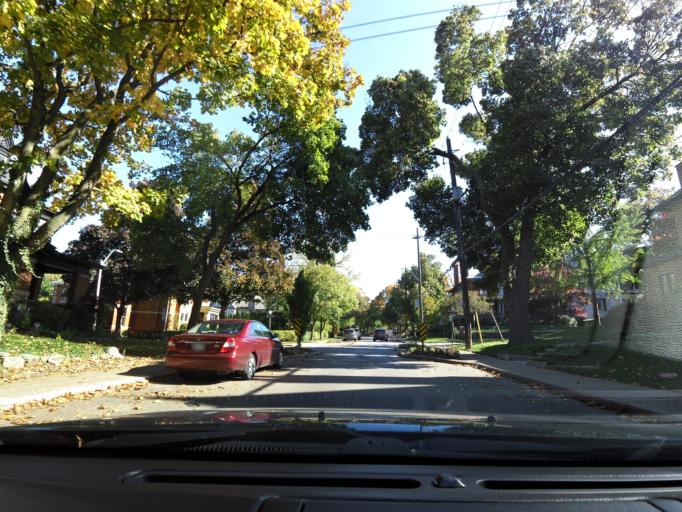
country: CA
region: Ontario
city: Hamilton
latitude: 43.2480
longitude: -79.8798
